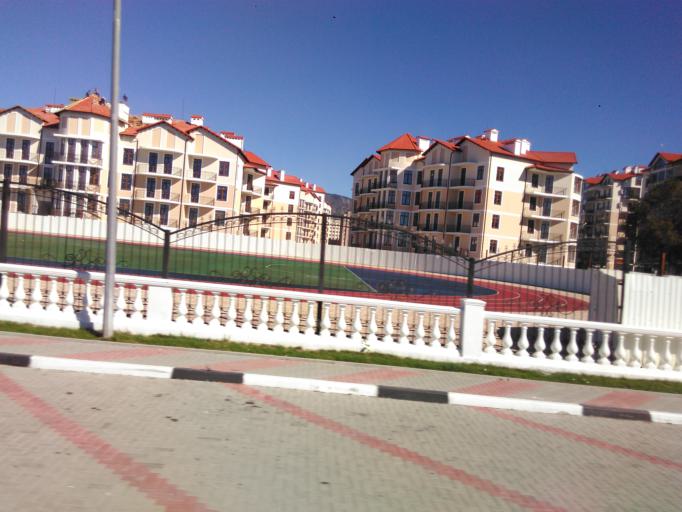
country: RU
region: Krasnodarskiy
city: Gelendzhik
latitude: 44.5474
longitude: 38.0578
